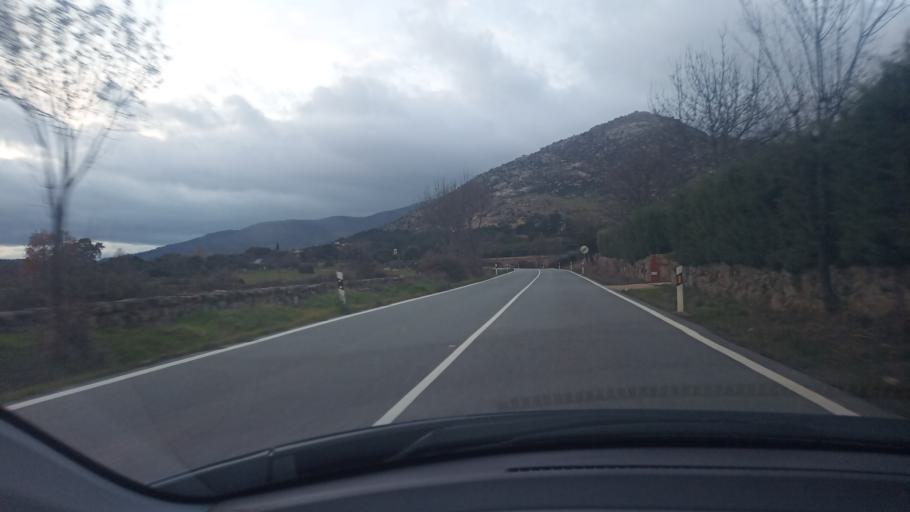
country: ES
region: Madrid
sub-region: Provincia de Madrid
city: Zarzalejo
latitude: 40.5394
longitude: -4.1396
